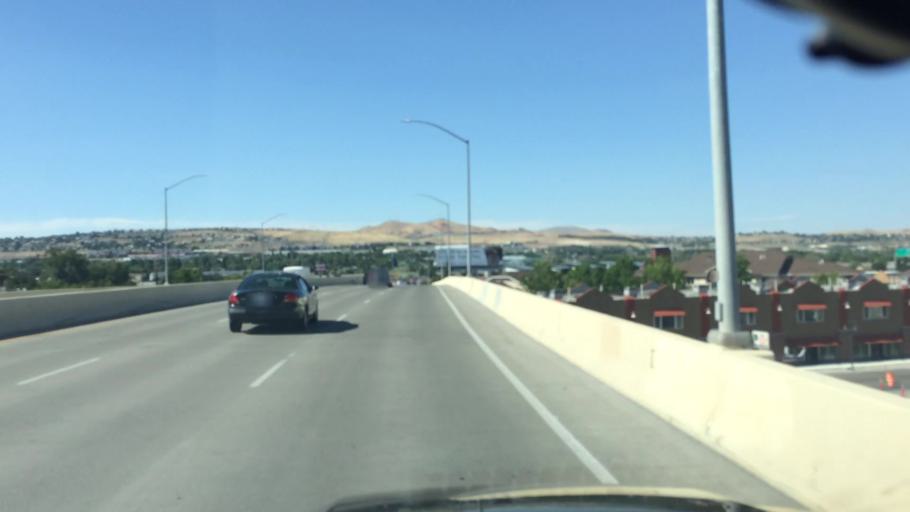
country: US
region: Nevada
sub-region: Washoe County
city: Reno
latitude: 39.5314
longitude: -119.8032
